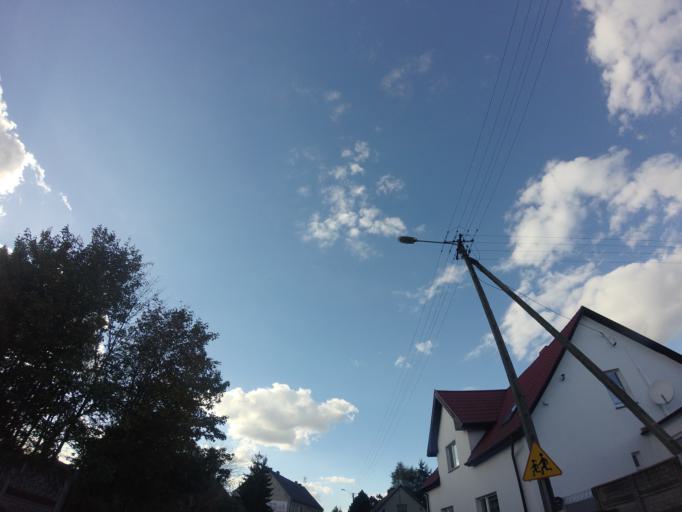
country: PL
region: Greater Poland Voivodeship
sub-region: Powiat nowotomyski
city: Nowy Tomysl
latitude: 52.2665
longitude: 16.1341
